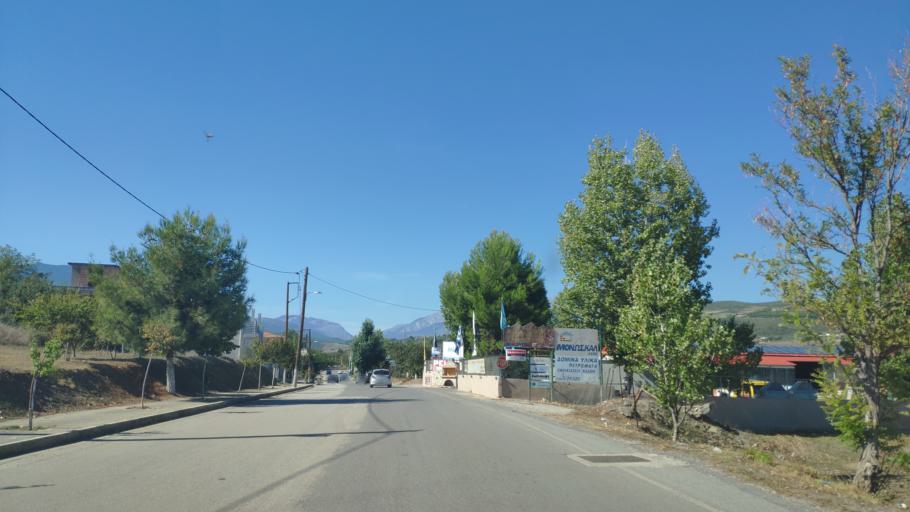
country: GR
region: Central Greece
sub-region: Nomos Voiotias
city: Livadeia
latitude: 38.4433
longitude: 22.8629
